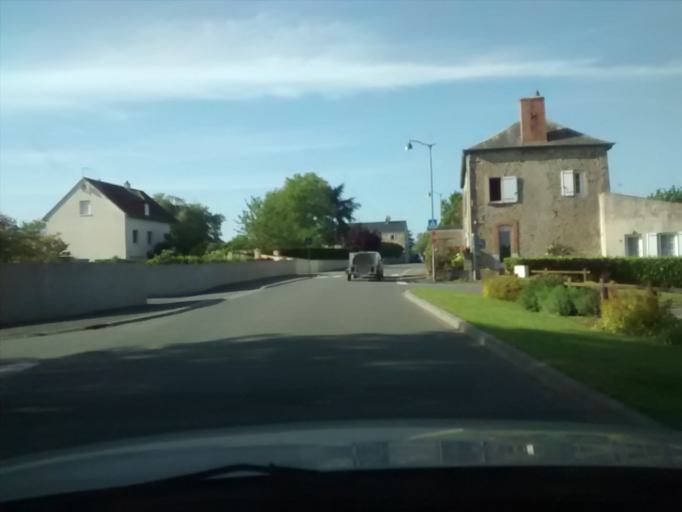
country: FR
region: Pays de la Loire
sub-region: Departement de la Mayenne
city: Soulge-sur-Ouette
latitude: 48.0203
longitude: -0.5813
